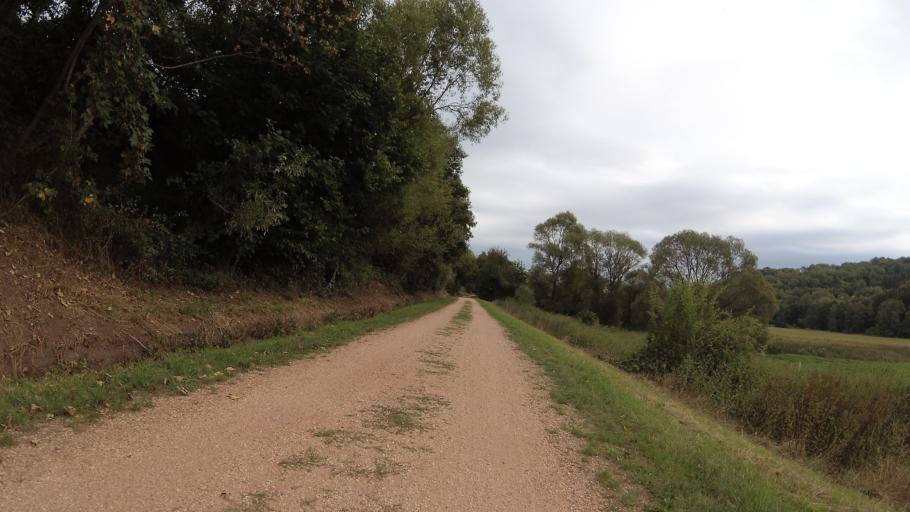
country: DE
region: Saarland
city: Wadern
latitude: 49.5255
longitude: 6.9237
